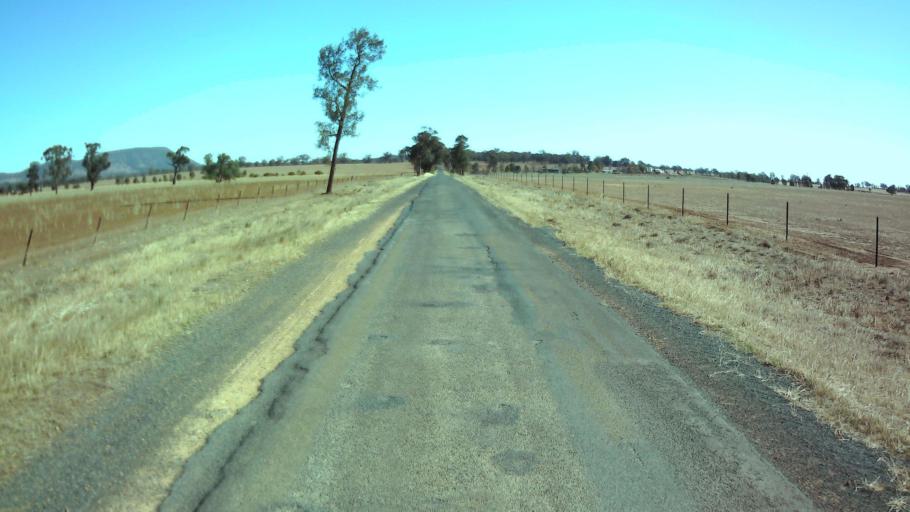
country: AU
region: New South Wales
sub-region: Weddin
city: Grenfell
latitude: -33.7987
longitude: 147.9562
